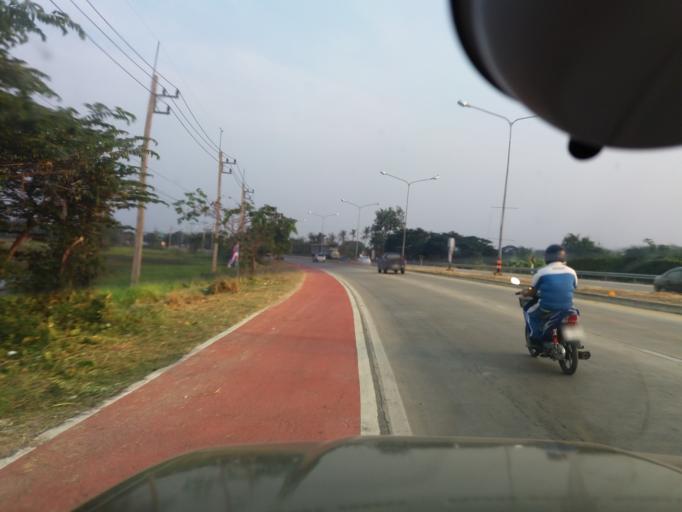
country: TH
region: Sing Buri
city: Sing Buri
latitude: 14.8723
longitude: 100.3973
